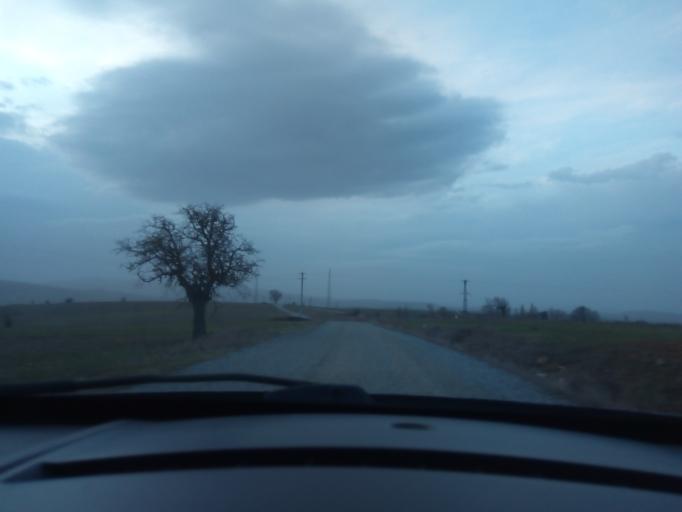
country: TR
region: Balikesir
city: Omerkoy
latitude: 39.8904
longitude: 28.0232
